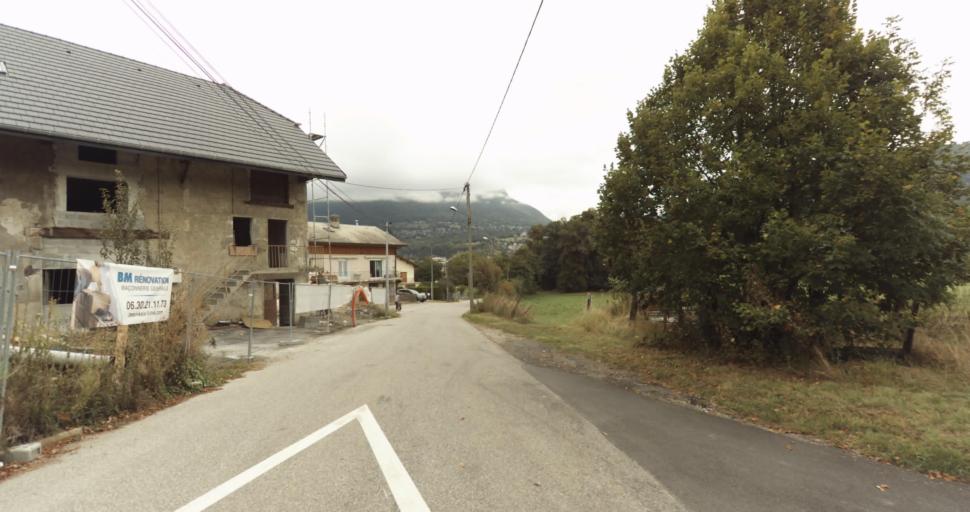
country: FR
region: Rhone-Alpes
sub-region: Departement de la Savoie
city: La Ravoire
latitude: 45.5657
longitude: 5.9613
